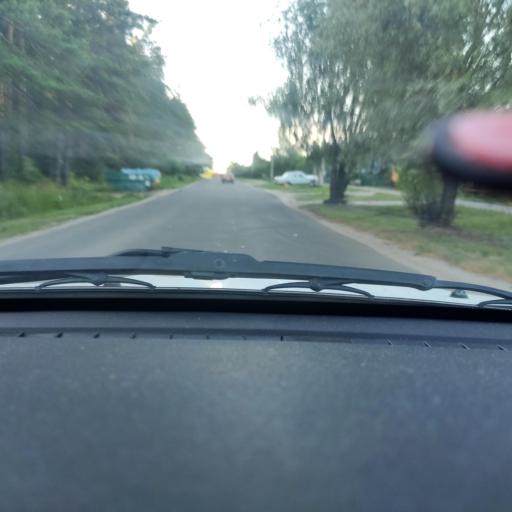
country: RU
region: Voronezj
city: Ramon'
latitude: 51.8972
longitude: 39.2852
